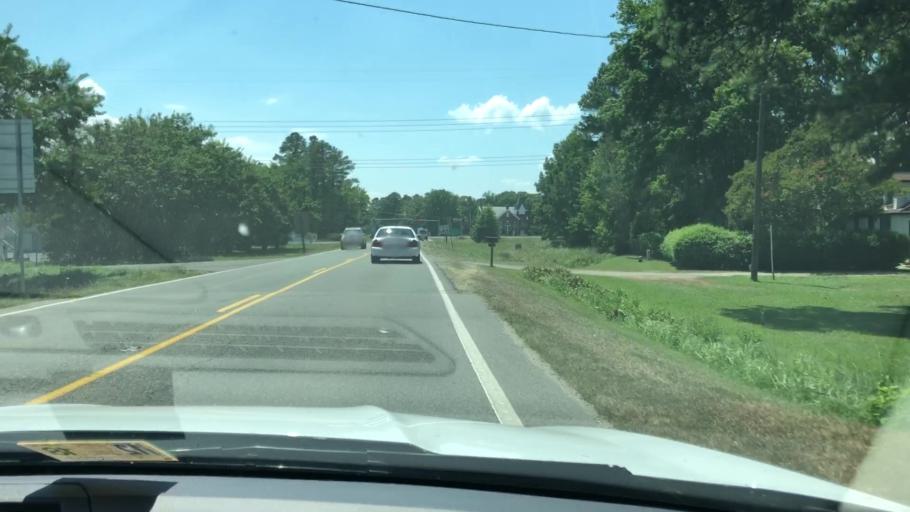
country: US
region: Virginia
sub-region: Middlesex County
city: Saluda
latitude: 37.5831
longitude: -76.4843
